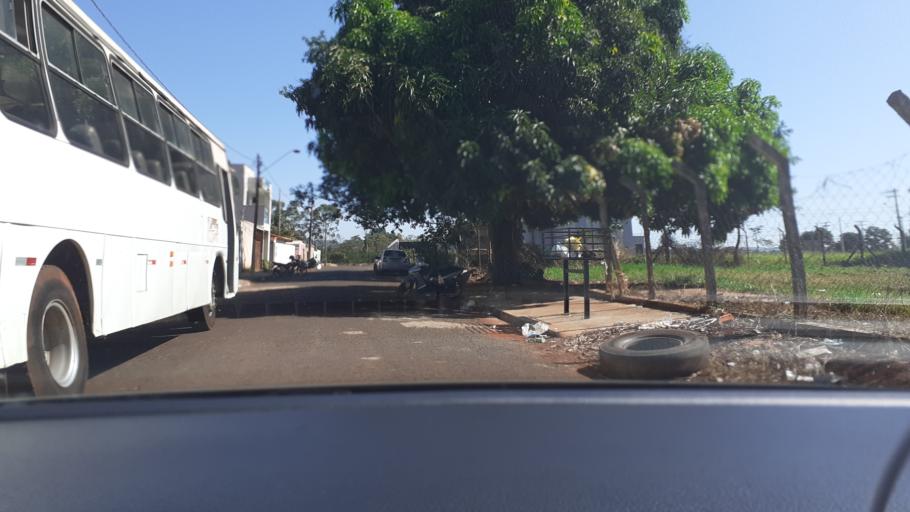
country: BR
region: Goias
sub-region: Itumbiara
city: Itumbiara
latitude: -18.4093
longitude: -49.2563
